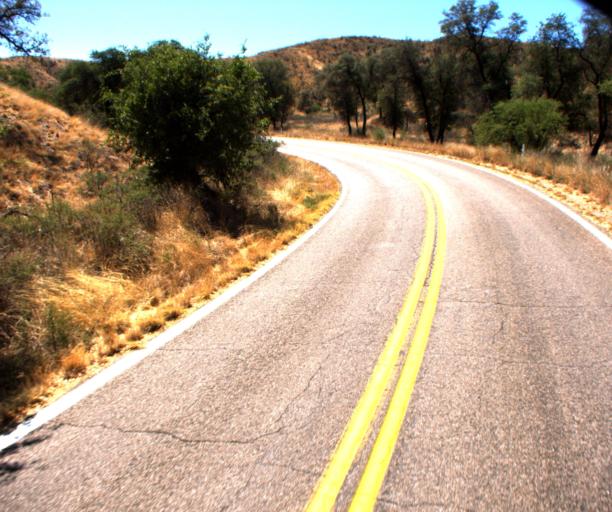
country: US
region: Arizona
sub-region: Santa Cruz County
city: Rio Rico
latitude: 31.3859
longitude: -111.0610
